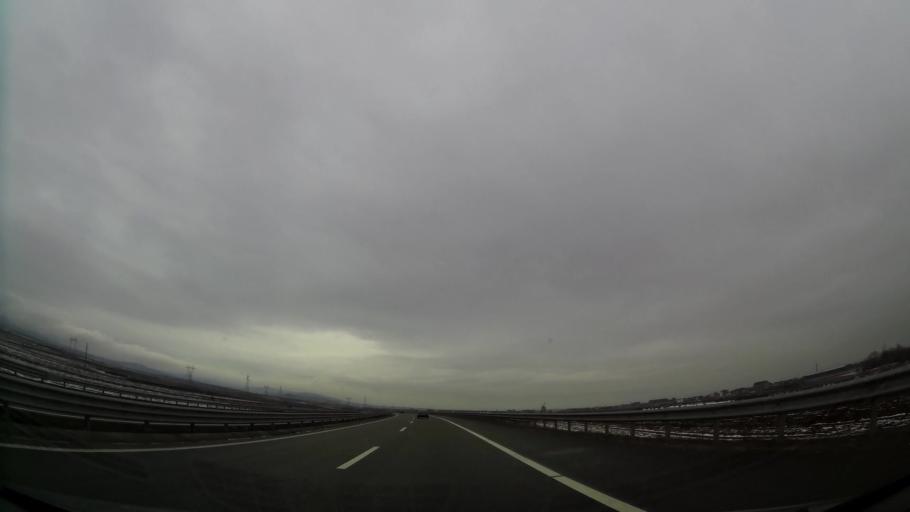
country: XK
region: Pristina
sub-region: Lipjan
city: Lipljan
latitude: 42.5228
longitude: 21.1676
